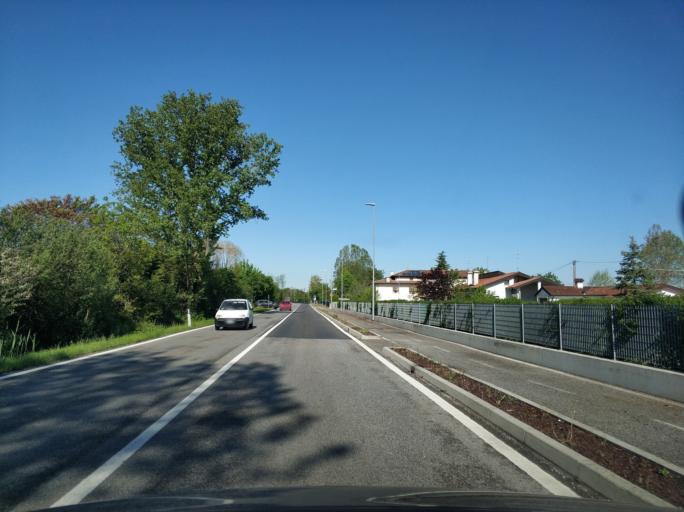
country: IT
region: Friuli Venezia Giulia
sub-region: Provincia di Udine
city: San Giorgio di Nogaro
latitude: 45.8276
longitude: 13.2327
